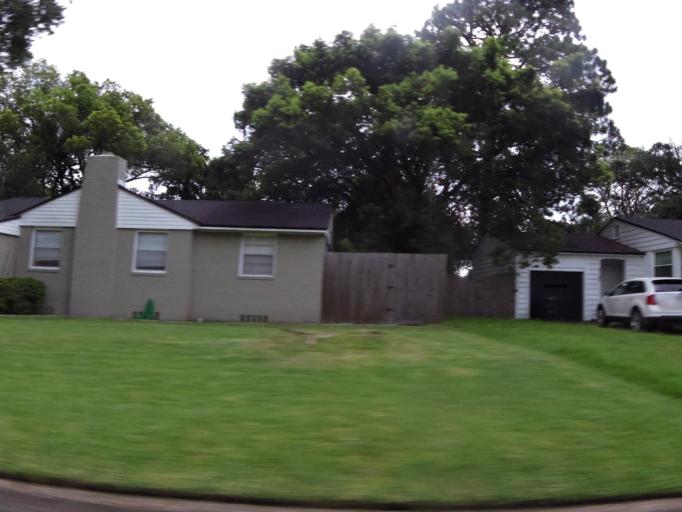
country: US
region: Florida
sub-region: Duval County
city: Jacksonville
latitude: 30.3034
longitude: -81.6370
